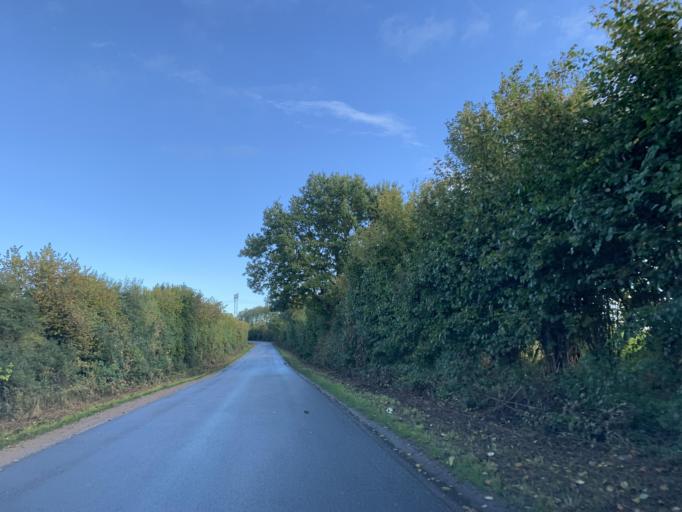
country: DE
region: Mecklenburg-Vorpommern
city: Blankensee
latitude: 53.4231
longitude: 13.2638
